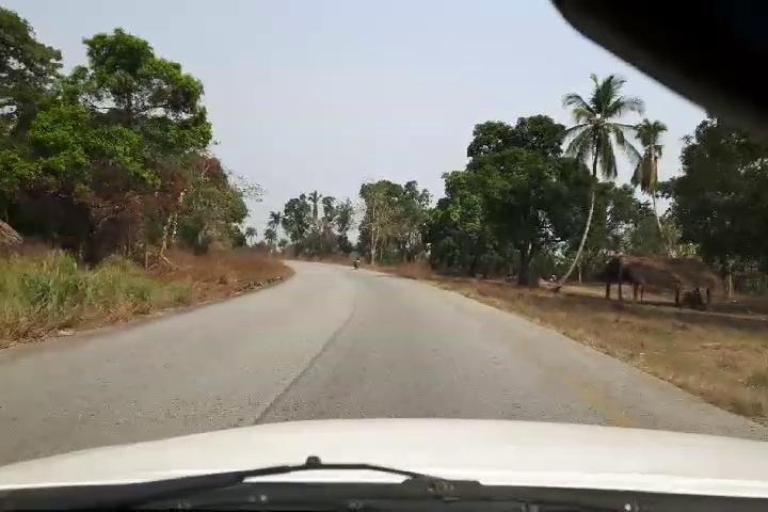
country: SL
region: Southern Province
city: Largo
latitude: 8.3090
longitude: -12.2109
